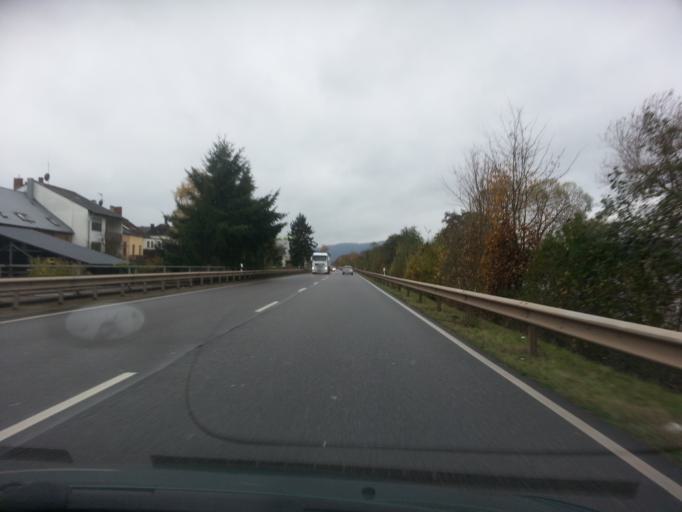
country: DE
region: Rheinland-Pfalz
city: Konz
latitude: 49.7131
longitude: 6.5968
